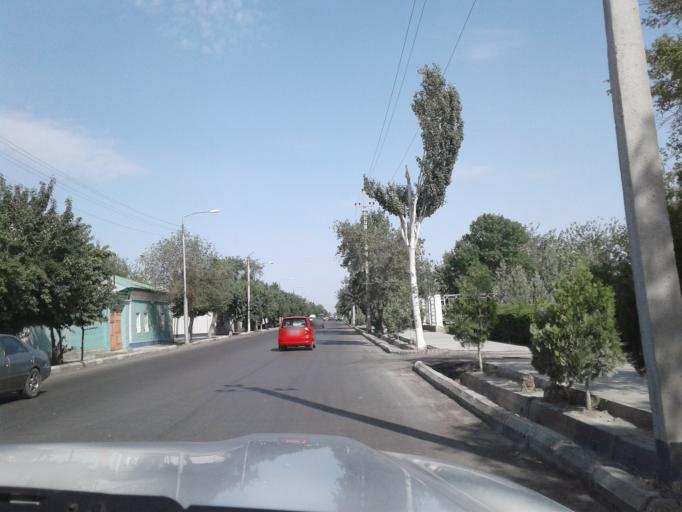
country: TM
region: Dasoguz
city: Dasoguz
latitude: 41.8340
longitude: 59.9487
